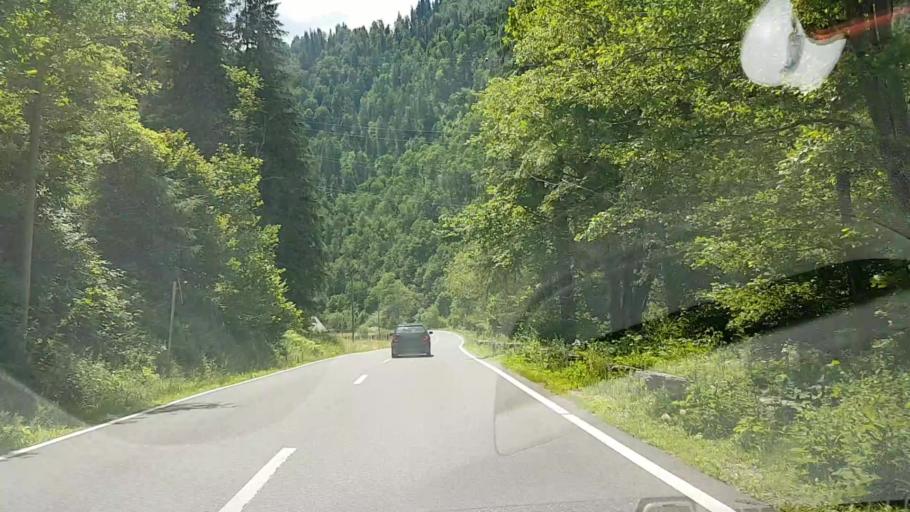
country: RO
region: Suceava
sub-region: Comuna Brosteni
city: Brosteni
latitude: 47.2770
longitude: 25.6492
